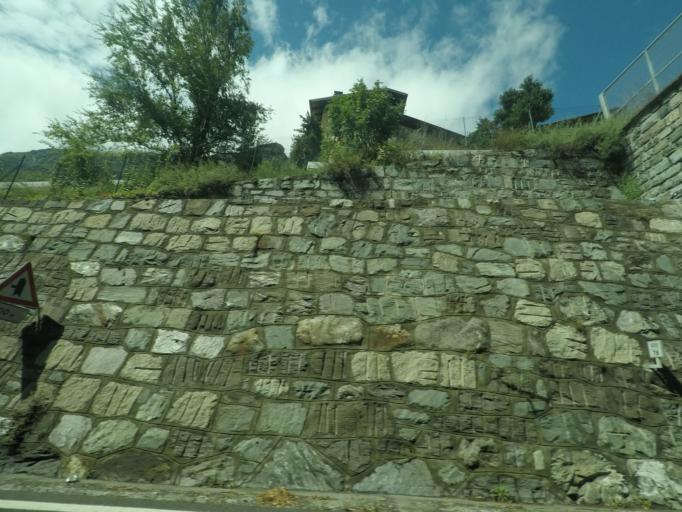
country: IT
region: Aosta Valley
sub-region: Valle d'Aosta
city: Lassolaz
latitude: 45.7464
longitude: 7.5992
